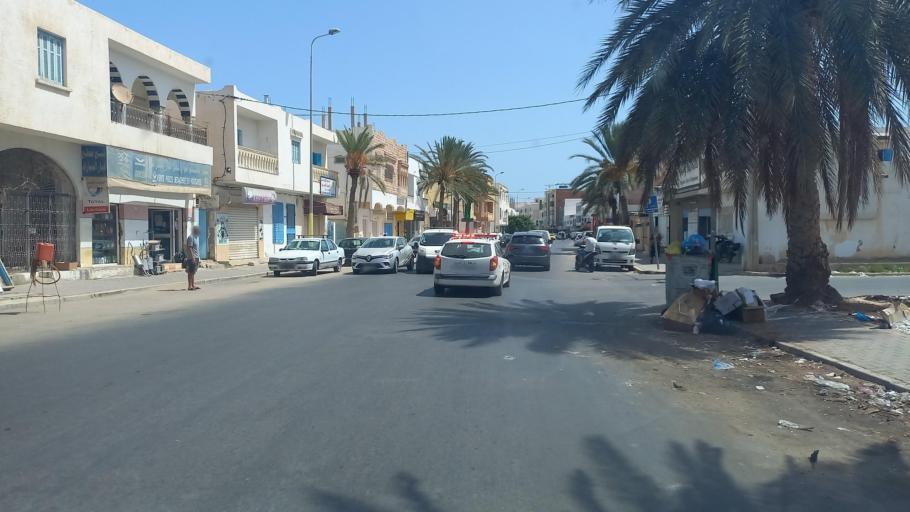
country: TN
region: Madanin
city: Zarzis
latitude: 33.5009
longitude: 11.1016
